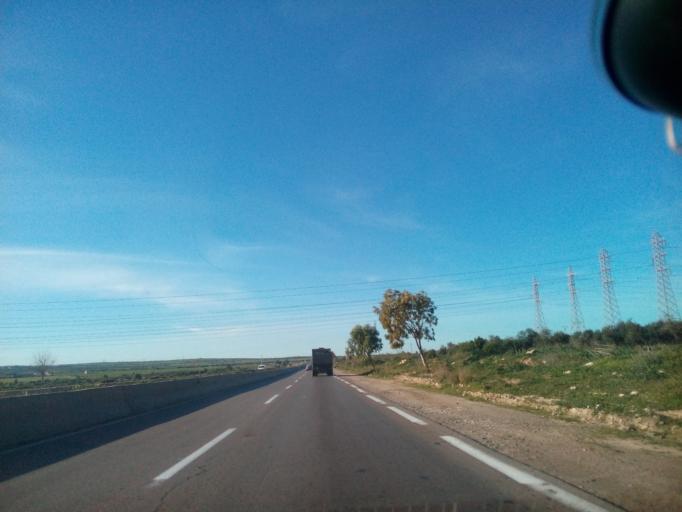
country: DZ
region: Oran
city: Ain el Bya
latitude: 35.7733
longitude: -0.1967
